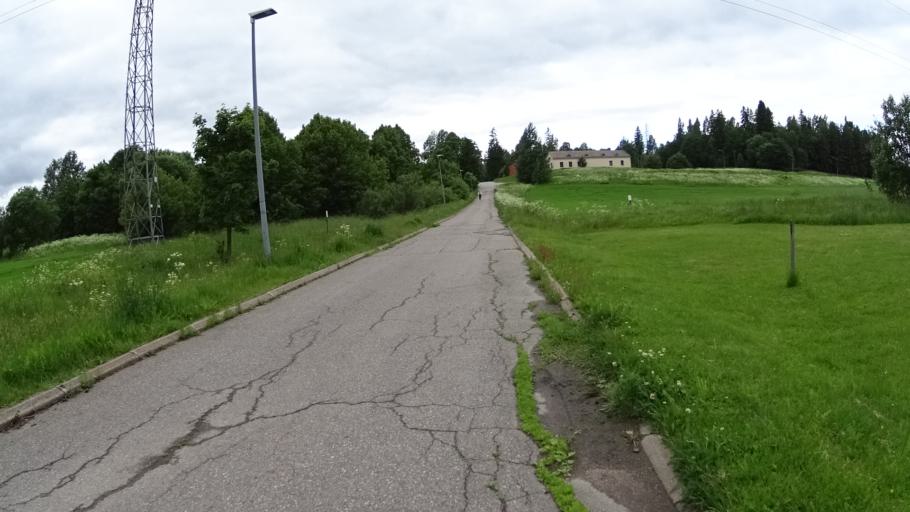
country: FI
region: Uusimaa
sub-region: Helsinki
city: Kilo
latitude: 60.2704
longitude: 24.7903
